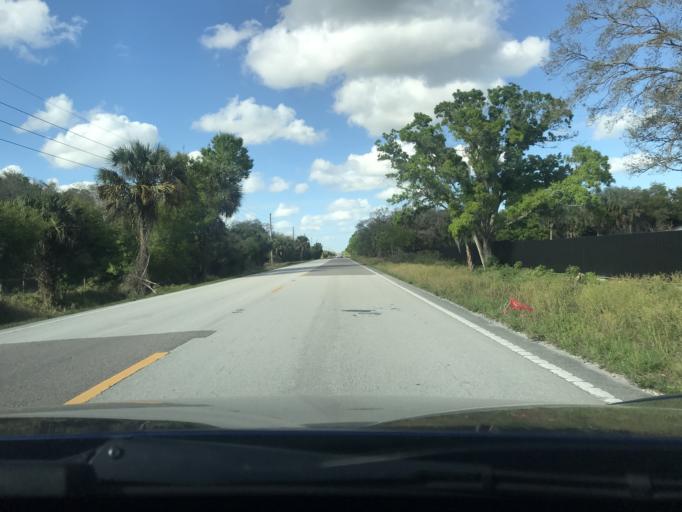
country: US
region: Florida
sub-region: Okeechobee County
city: Taylor Creek
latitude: 27.2074
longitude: -80.6941
